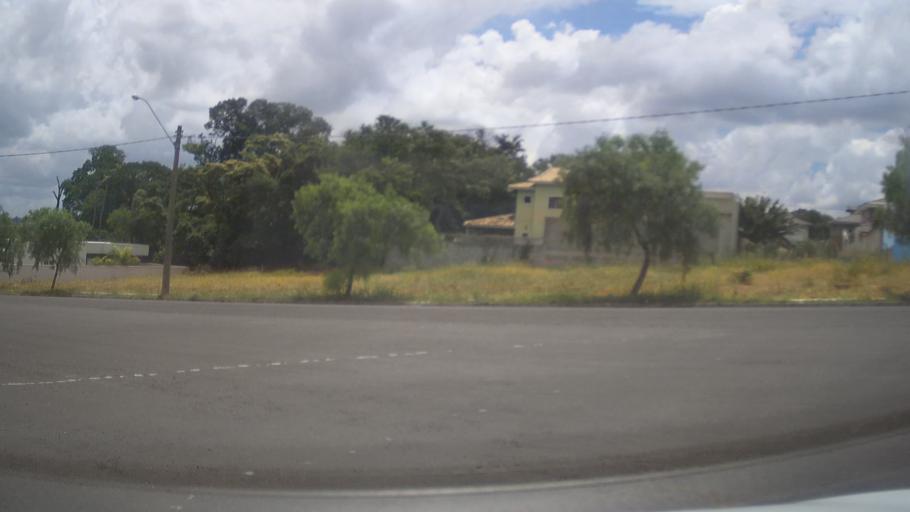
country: BR
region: Sao Paulo
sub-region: Itupeva
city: Itupeva
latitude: -23.1696
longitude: -47.0052
